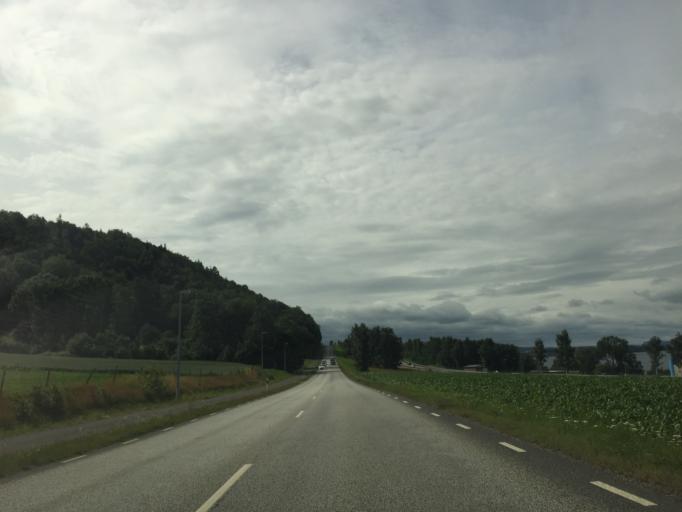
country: SE
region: Joenkoeping
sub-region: Jonkopings Kommun
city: Kaxholmen
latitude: 57.8327
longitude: 14.2716
